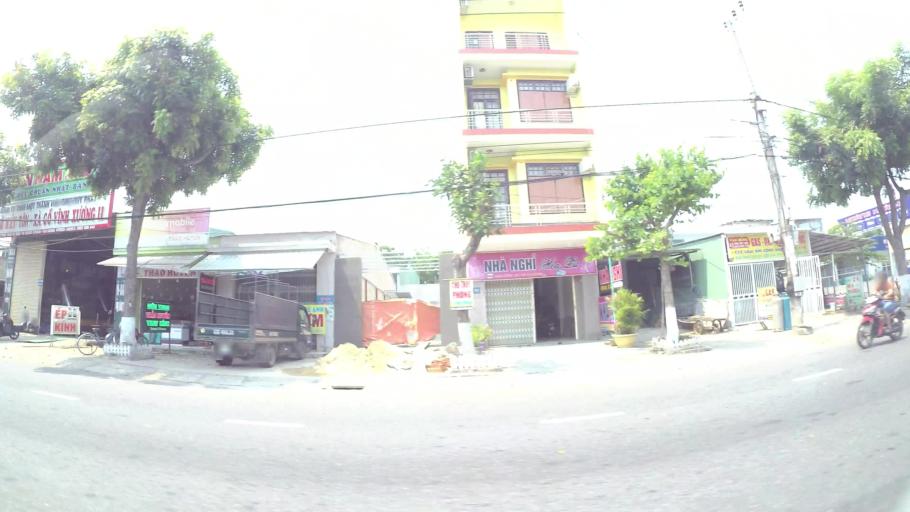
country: VN
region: Da Nang
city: Cam Le
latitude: 15.9853
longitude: 108.2079
